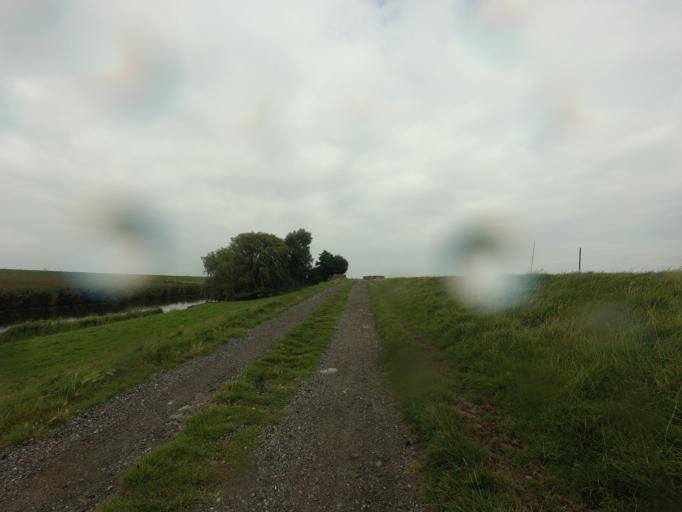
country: NL
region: Friesland
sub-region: Sudwest Fryslan
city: Koudum
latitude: 52.9048
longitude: 5.3921
